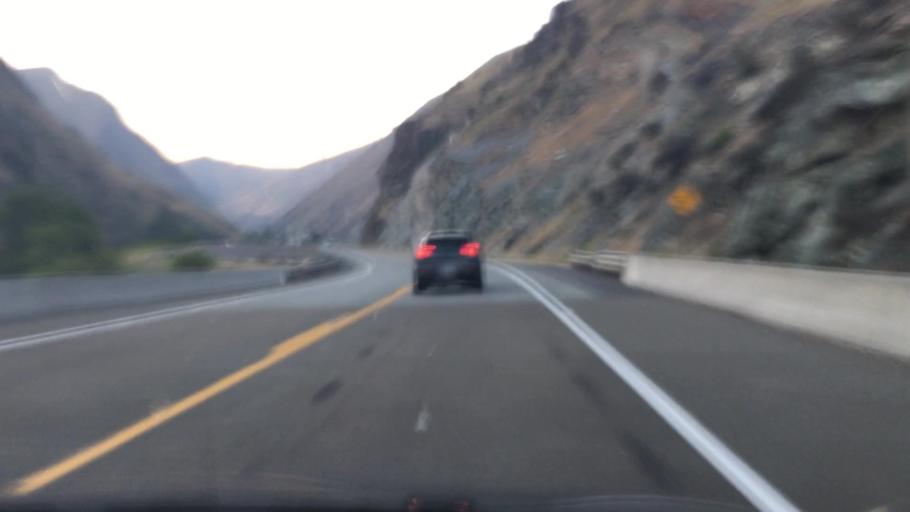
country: US
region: Idaho
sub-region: Idaho County
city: Grangeville
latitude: 45.4455
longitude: -116.3112
